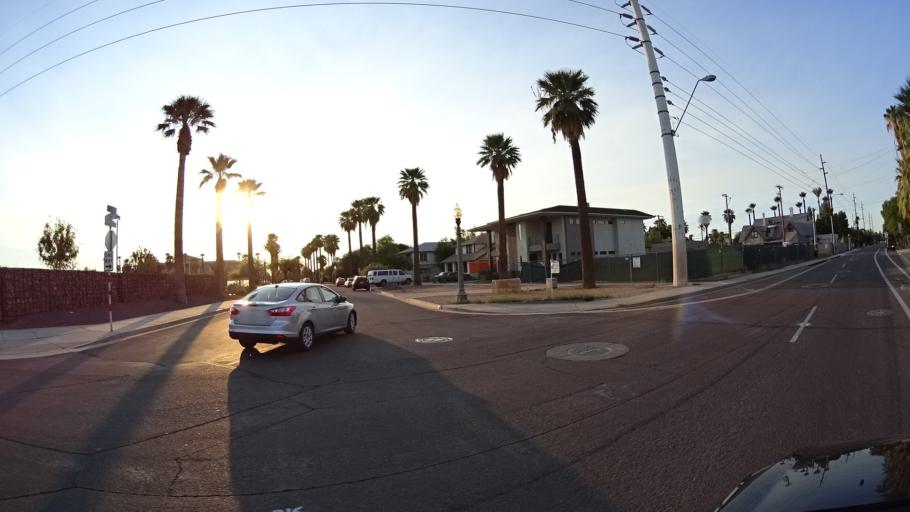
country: US
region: Arizona
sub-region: Maricopa County
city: Phoenix
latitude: 33.4625
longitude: -112.0781
